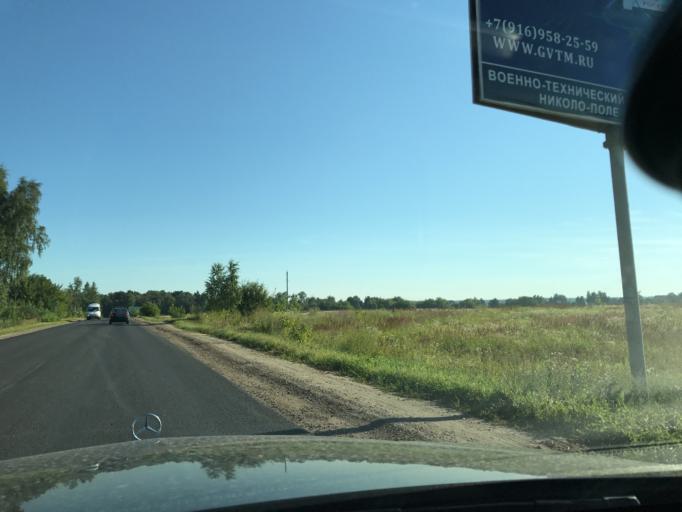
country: RU
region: Moskovskaya
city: Sverdlovskiy
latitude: 55.8835
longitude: 38.1621
